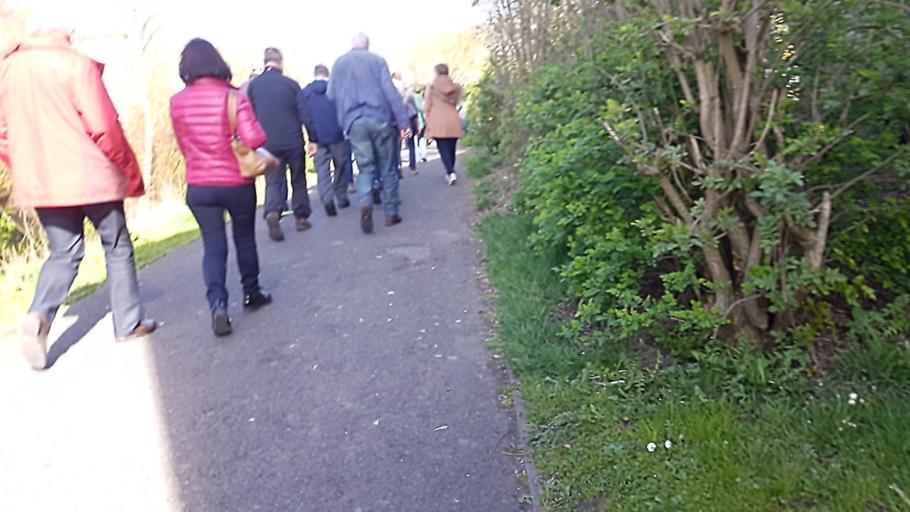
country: BE
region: Flanders
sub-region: Provincie West-Vlaanderen
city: Kortrijk
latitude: 50.8165
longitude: 3.2846
